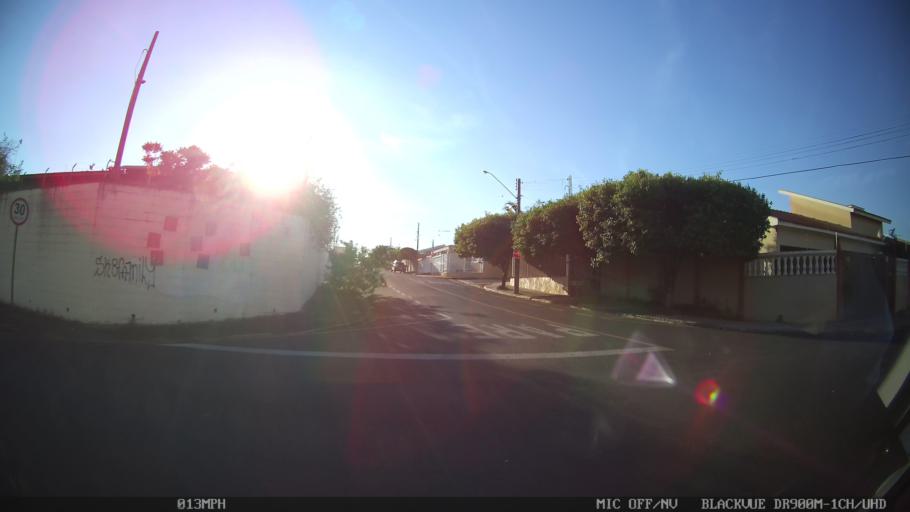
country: BR
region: Sao Paulo
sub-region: Sao Jose Do Rio Preto
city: Sao Jose do Rio Preto
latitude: -20.7973
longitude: -49.3616
